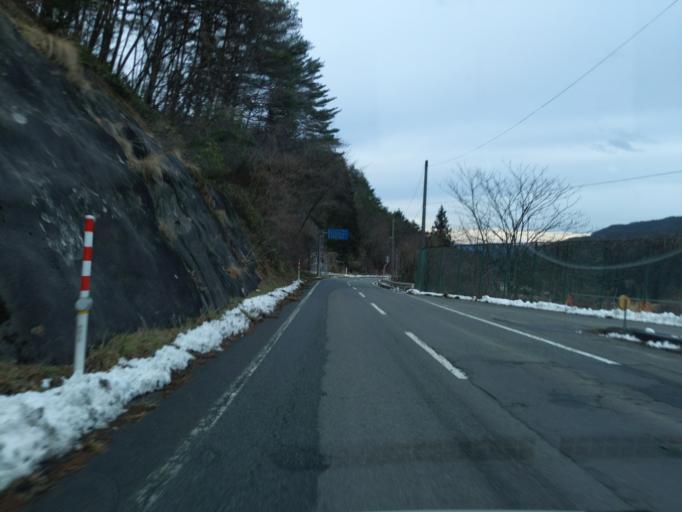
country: JP
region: Iwate
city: Mizusawa
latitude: 39.0859
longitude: 141.2755
